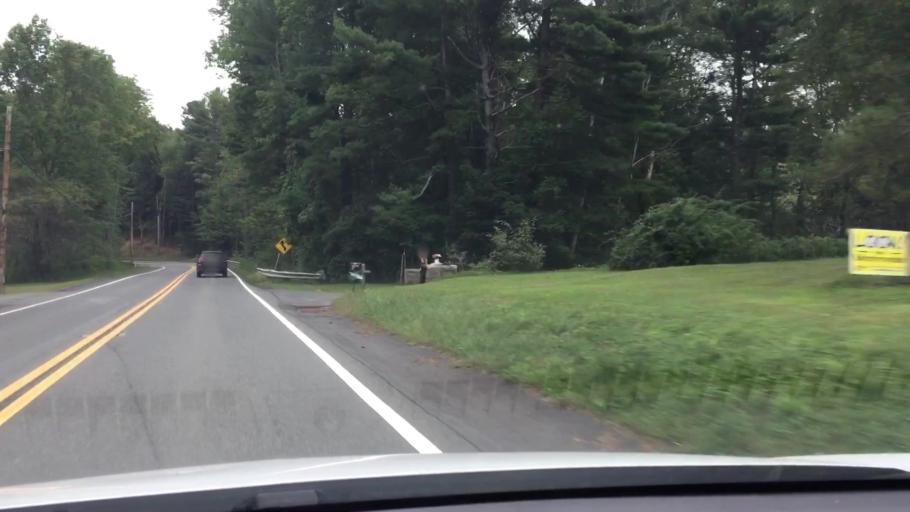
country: US
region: Massachusetts
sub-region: Berkshire County
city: Becket
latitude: 42.3702
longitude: -73.1165
